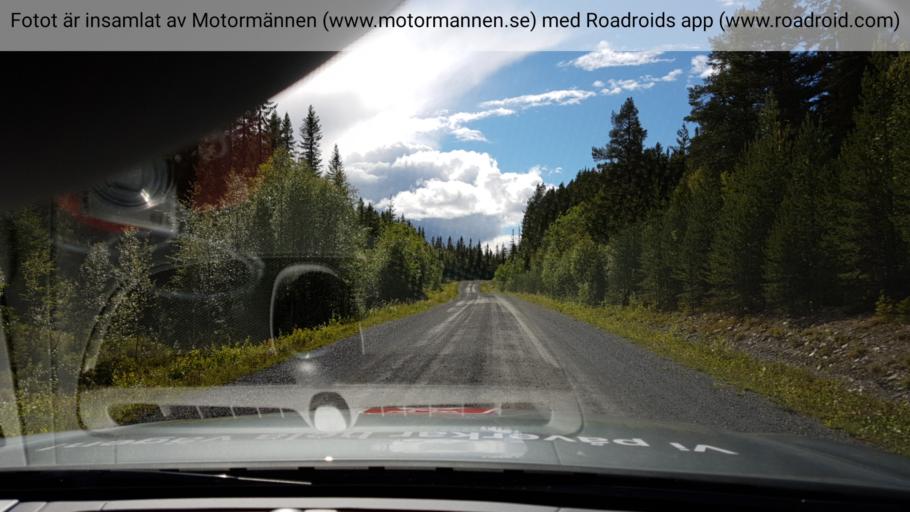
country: SE
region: Jaemtland
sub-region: Krokoms Kommun
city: Valla
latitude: 63.0805
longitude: 13.9501
